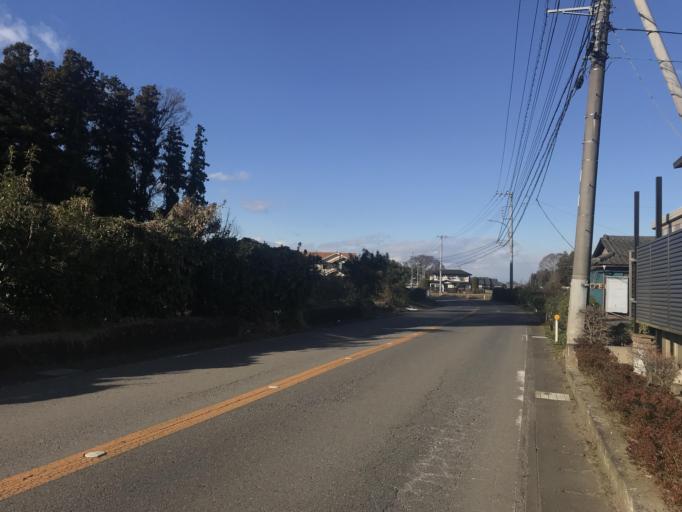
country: JP
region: Tochigi
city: Kaminokawa
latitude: 36.4167
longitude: 139.8776
